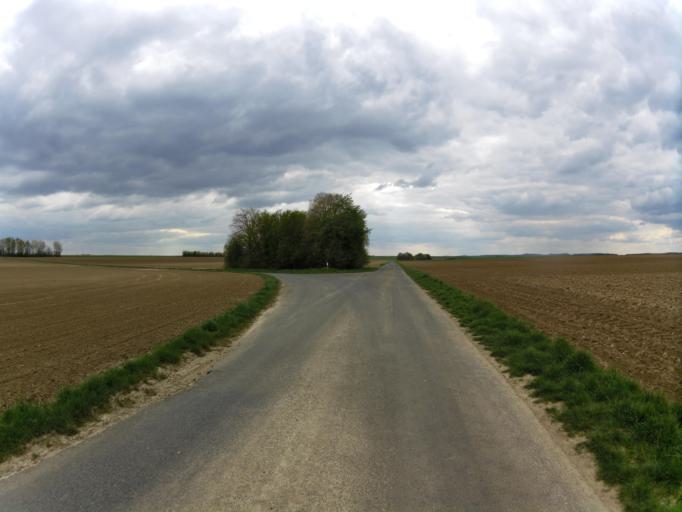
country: DE
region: Bavaria
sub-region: Regierungsbezirk Unterfranken
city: Giebelstadt
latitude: 49.6455
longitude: 9.9364
